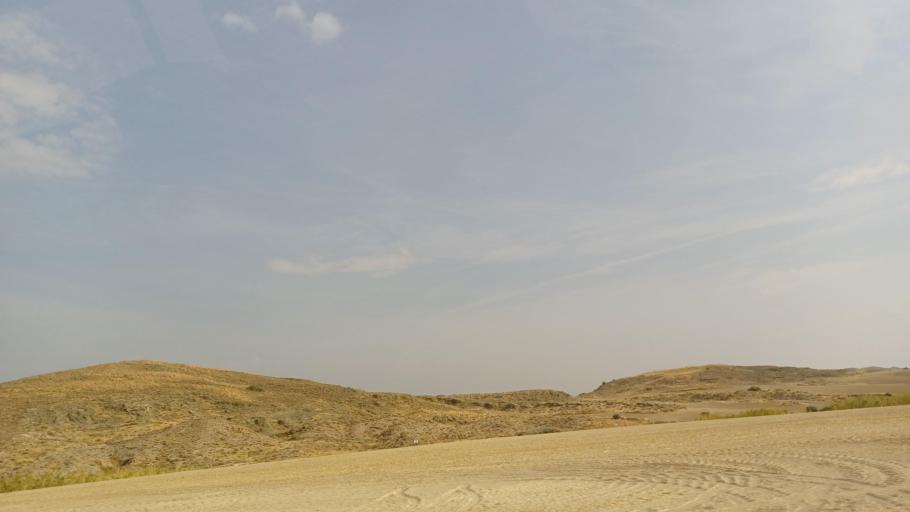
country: CY
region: Larnaka
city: Troulloi
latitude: 35.0010
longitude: 33.5747
